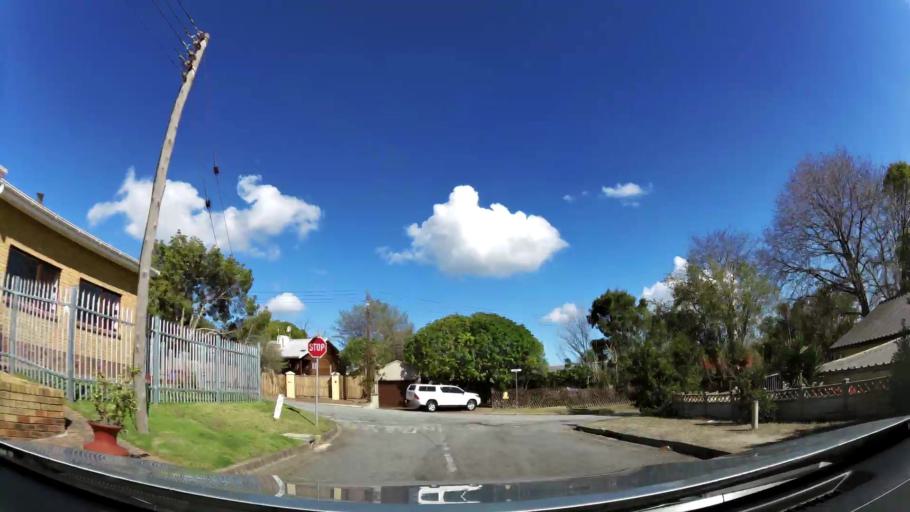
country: ZA
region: Western Cape
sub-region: Eden District Municipality
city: George
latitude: -33.9679
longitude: 22.4467
